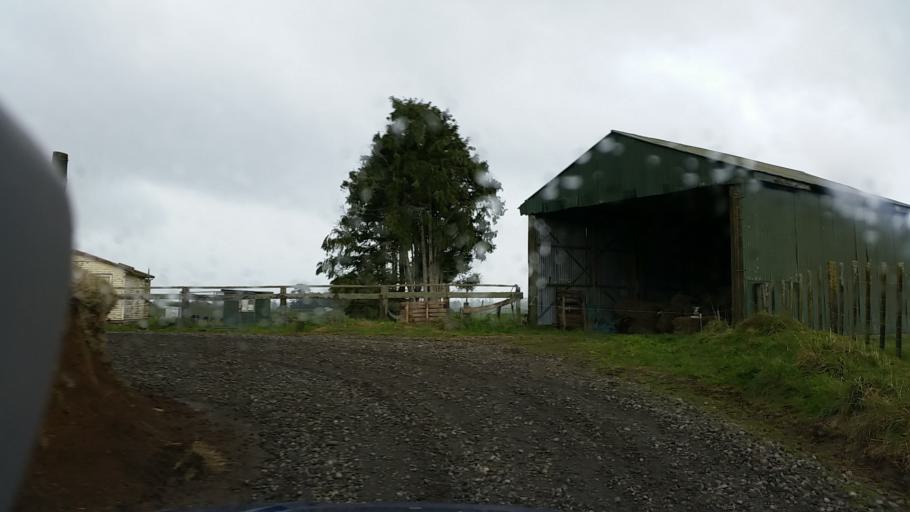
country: NZ
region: Taranaki
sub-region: South Taranaki District
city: Eltham
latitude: -39.2747
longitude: 174.3388
